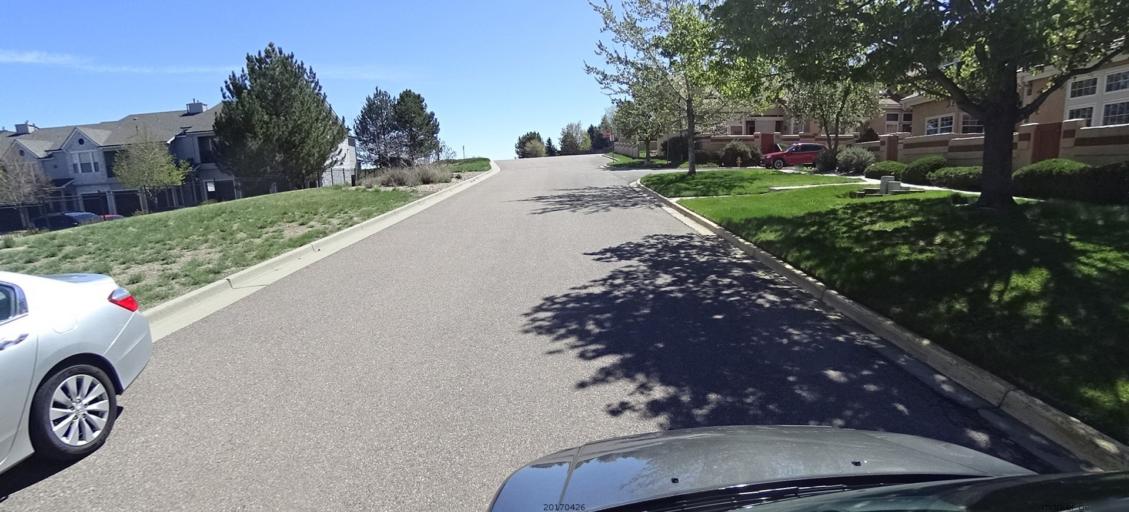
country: US
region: Colorado
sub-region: Adams County
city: Lone Tree
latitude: 39.5508
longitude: -104.8866
